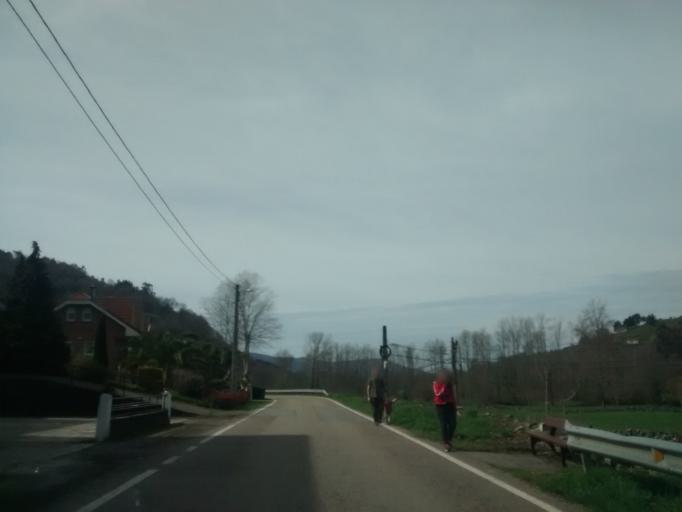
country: ES
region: Cantabria
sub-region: Provincia de Cantabria
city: Santiurde de Toranzo
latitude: 43.1691
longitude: -3.8960
